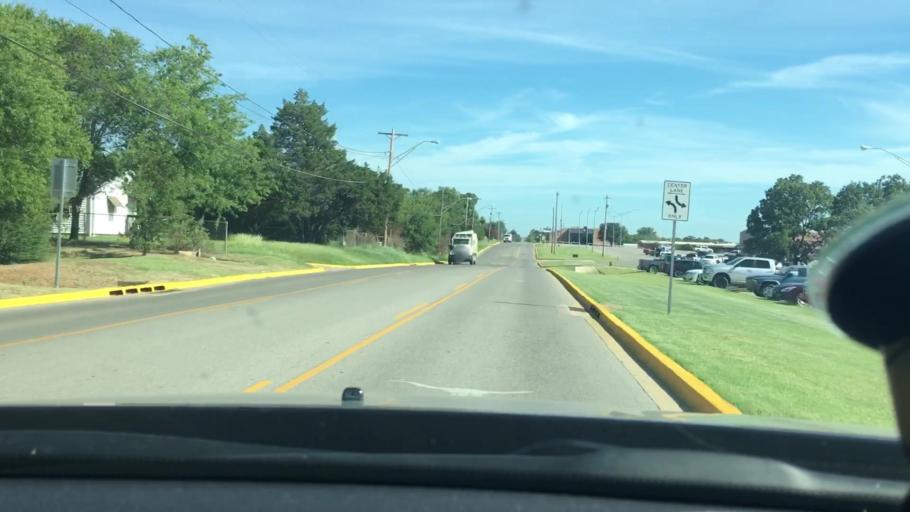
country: US
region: Oklahoma
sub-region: Carter County
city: Lone Grove
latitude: 34.1749
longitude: -97.2474
